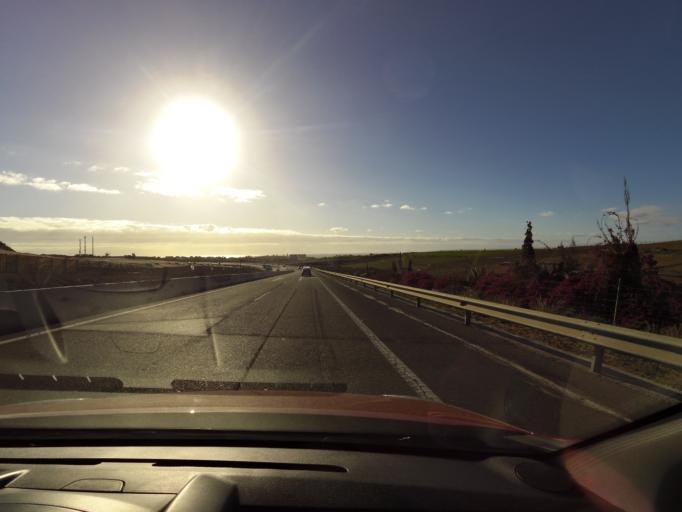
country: ES
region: Canary Islands
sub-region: Provincia de Las Palmas
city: Maspalomas
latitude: 27.7598
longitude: -15.6230
